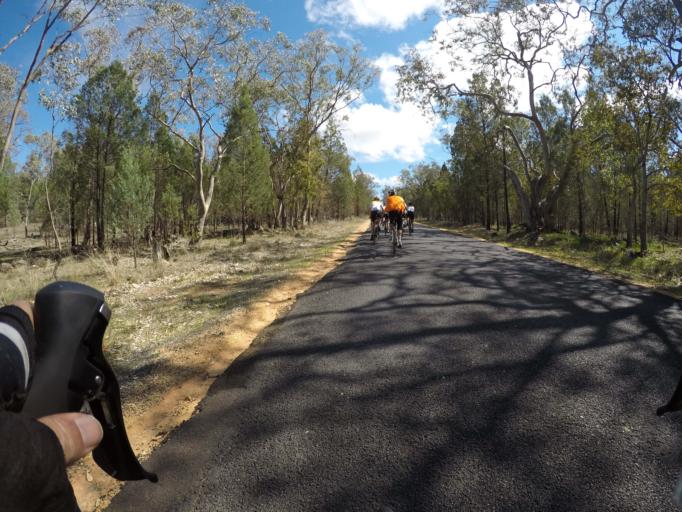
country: AU
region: New South Wales
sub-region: Parkes
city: Peak Hill
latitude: -32.6454
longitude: 148.5509
